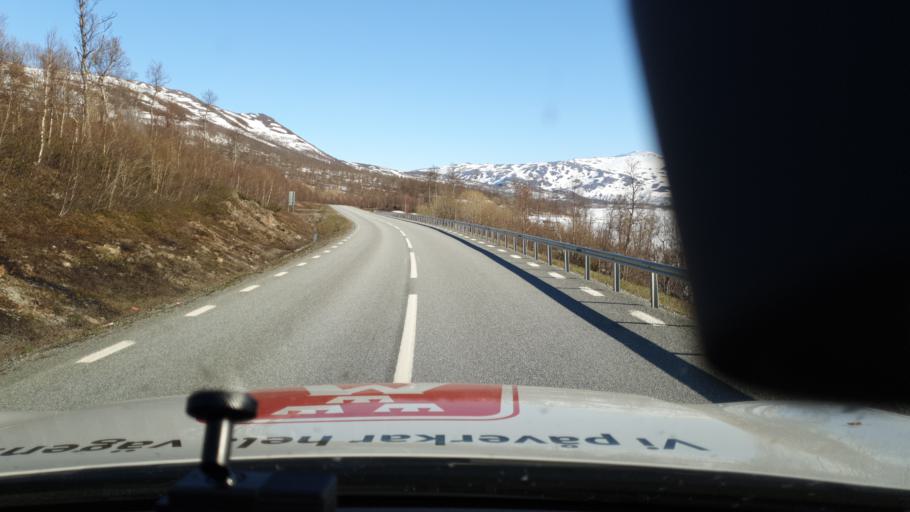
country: NO
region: Nordland
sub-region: Rana
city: Mo i Rana
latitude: 66.0936
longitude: 14.8523
